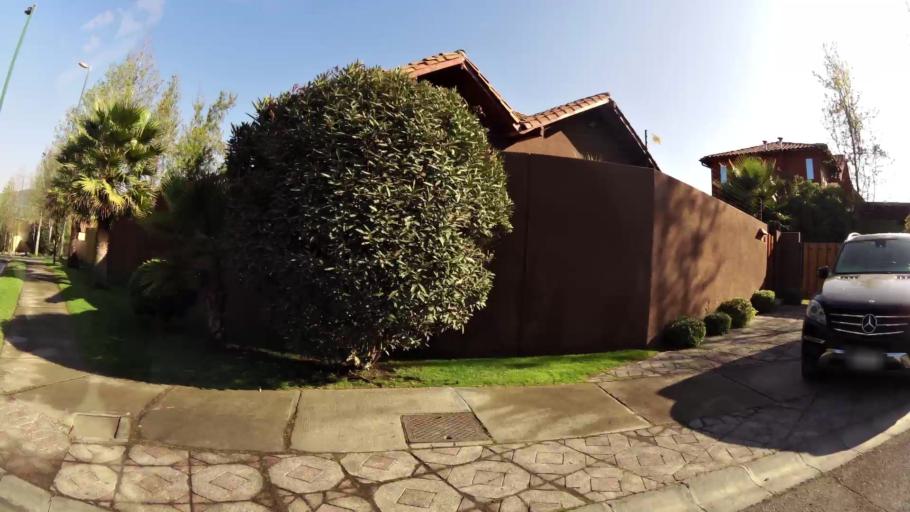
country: CL
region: Santiago Metropolitan
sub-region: Provincia de Chacabuco
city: Chicureo Abajo
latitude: -33.3479
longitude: -70.6649
